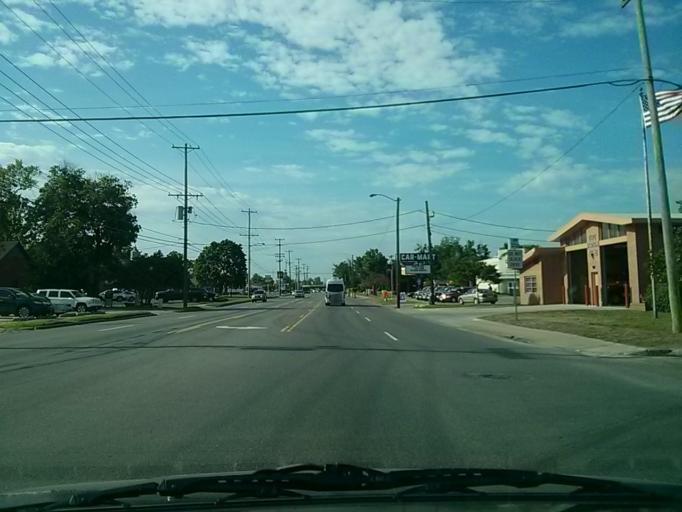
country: US
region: Oklahoma
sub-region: Tulsa County
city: Tulsa
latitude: 36.0948
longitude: -95.9758
